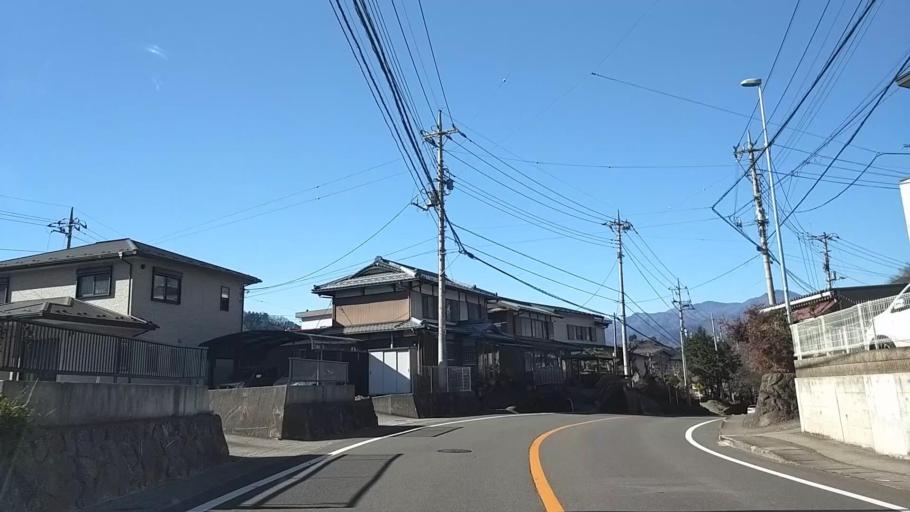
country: JP
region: Yamanashi
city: Otsuki
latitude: 35.6090
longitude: 138.9993
